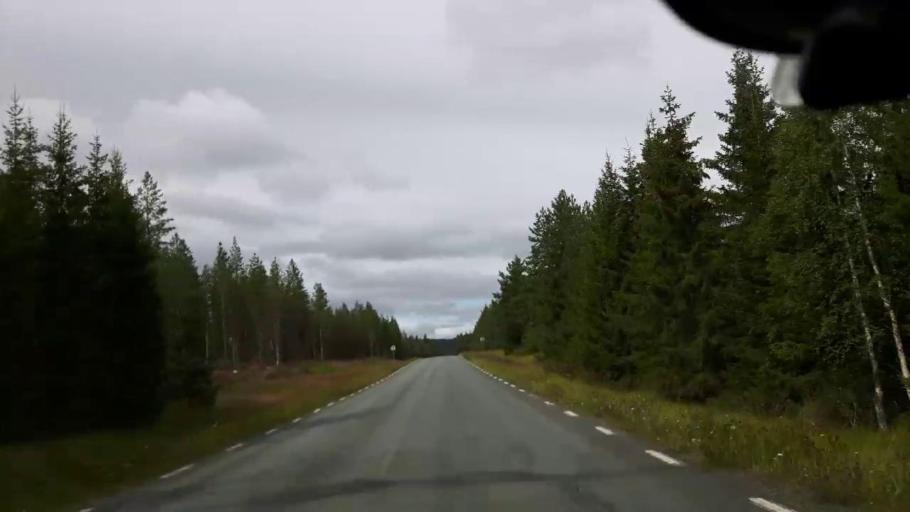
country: SE
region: Jaemtland
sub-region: Krokoms Kommun
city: Valla
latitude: 63.4756
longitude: 13.9951
